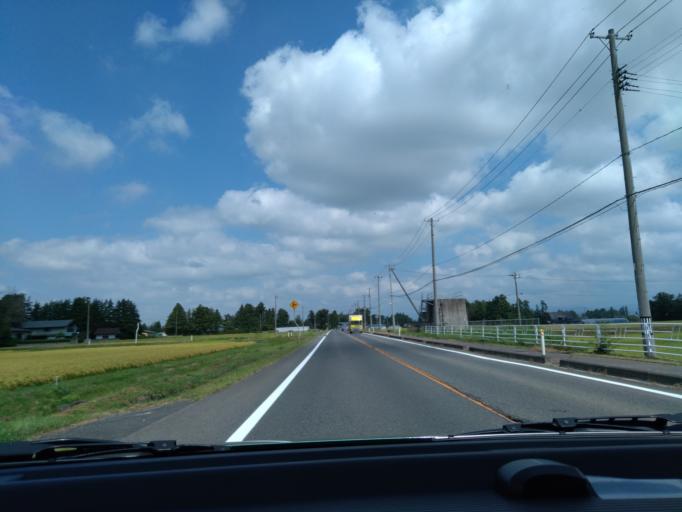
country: JP
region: Iwate
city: Hanamaki
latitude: 39.4285
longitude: 141.0903
